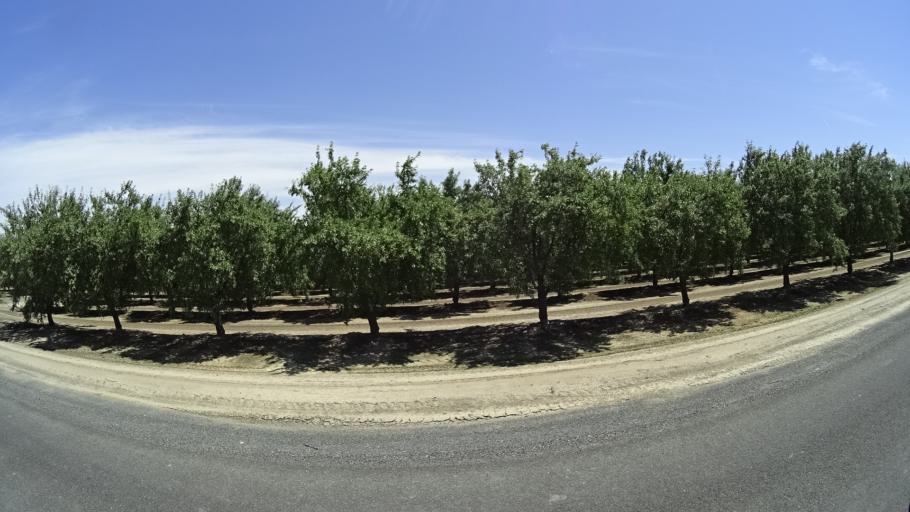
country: US
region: California
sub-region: Kings County
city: Armona
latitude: 36.3315
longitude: -119.7181
